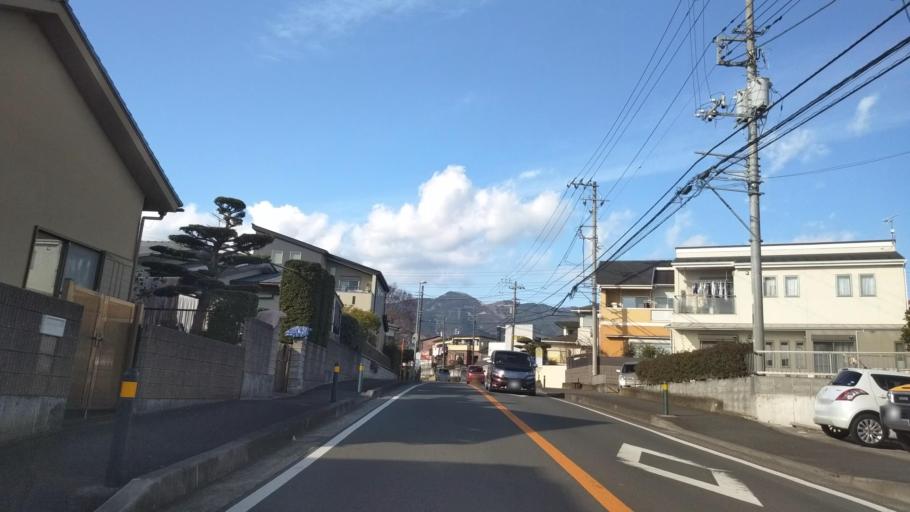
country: JP
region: Kanagawa
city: Hadano
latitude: 35.3855
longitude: 139.2372
